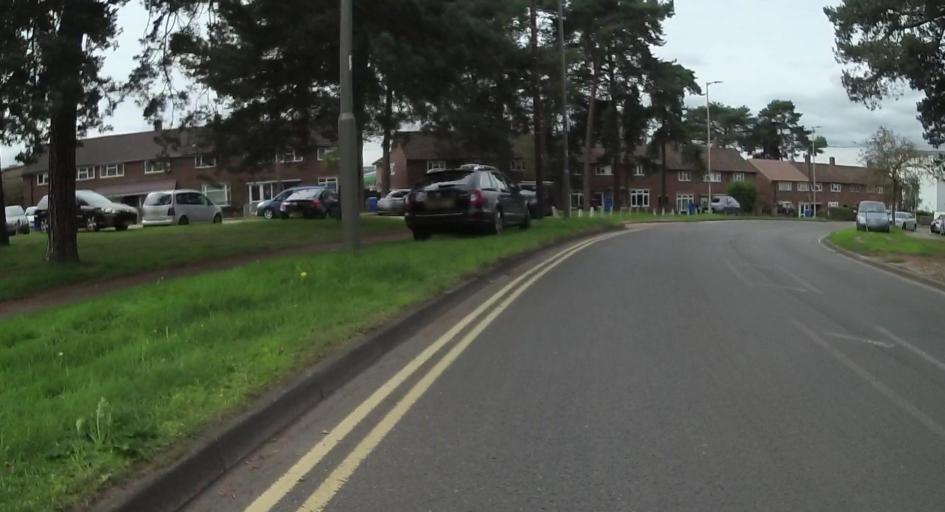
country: GB
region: England
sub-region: Surrey
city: West Byfleet
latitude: 51.3313
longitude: -0.5290
